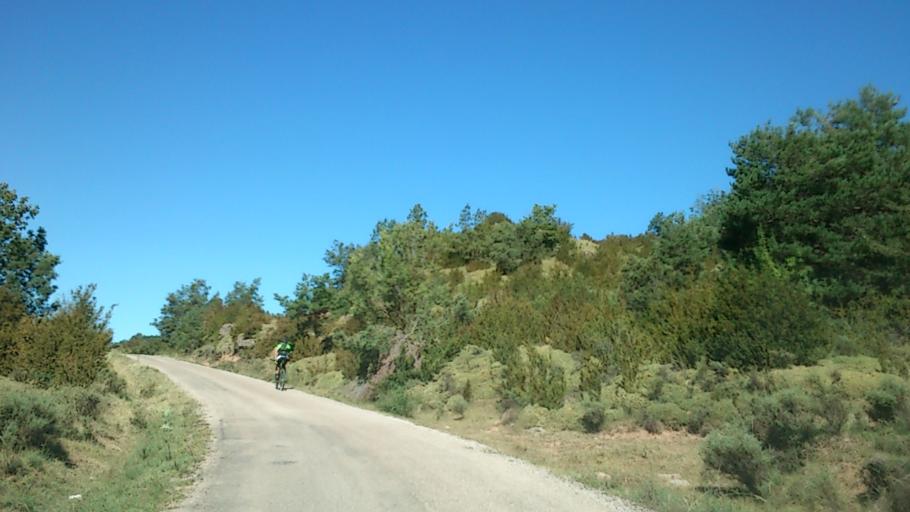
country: ES
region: Aragon
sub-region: Provincia de Huesca
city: Arguis
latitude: 42.3181
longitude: -0.2794
